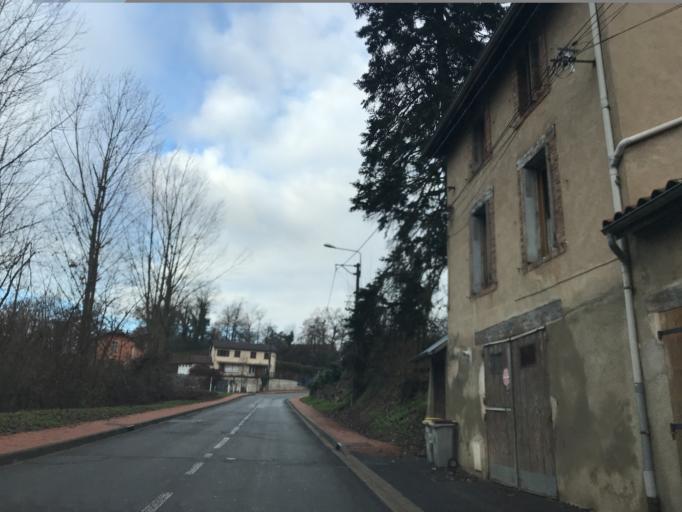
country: FR
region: Auvergne
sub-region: Departement du Puy-de-Dome
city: Thiers
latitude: 45.8520
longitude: 3.5343
